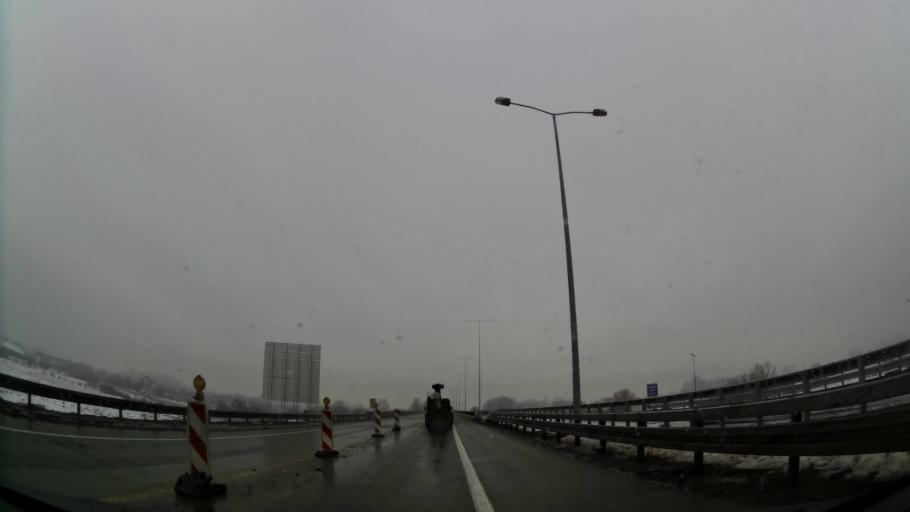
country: RS
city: Ostruznica
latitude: 44.7357
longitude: 20.3301
